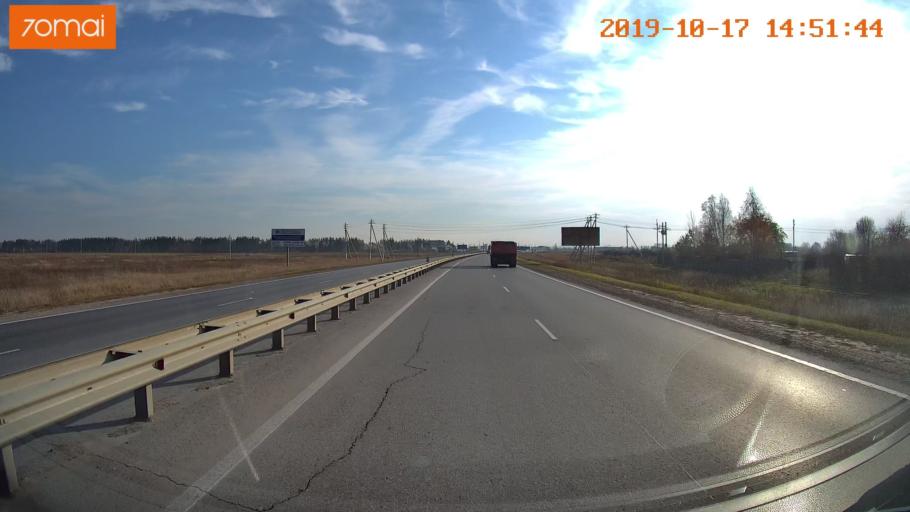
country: RU
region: Rjazan
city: Polyany
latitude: 54.7146
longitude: 39.8481
